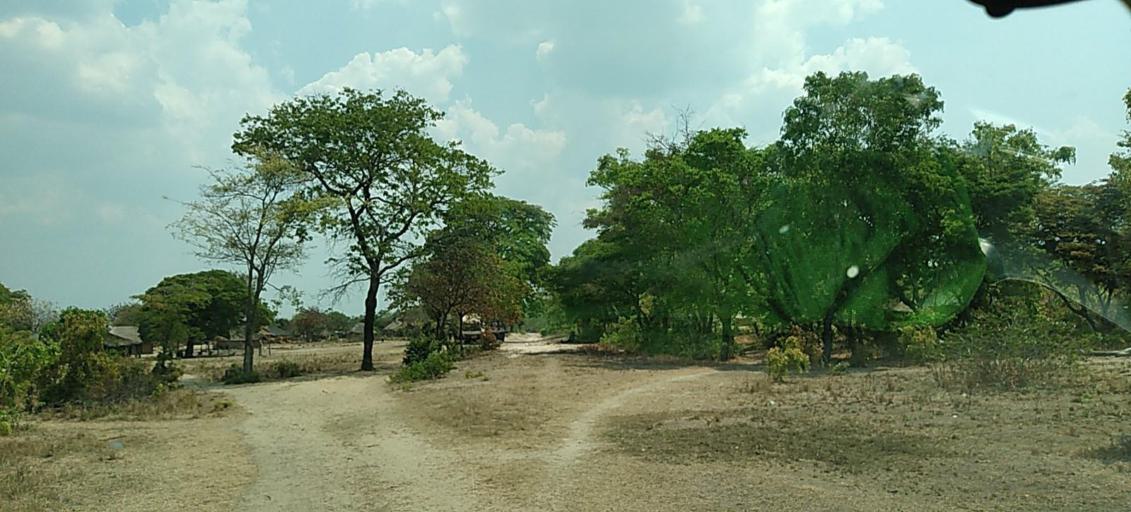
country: ZM
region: North-Western
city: Kabompo
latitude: -13.3576
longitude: 23.8927
